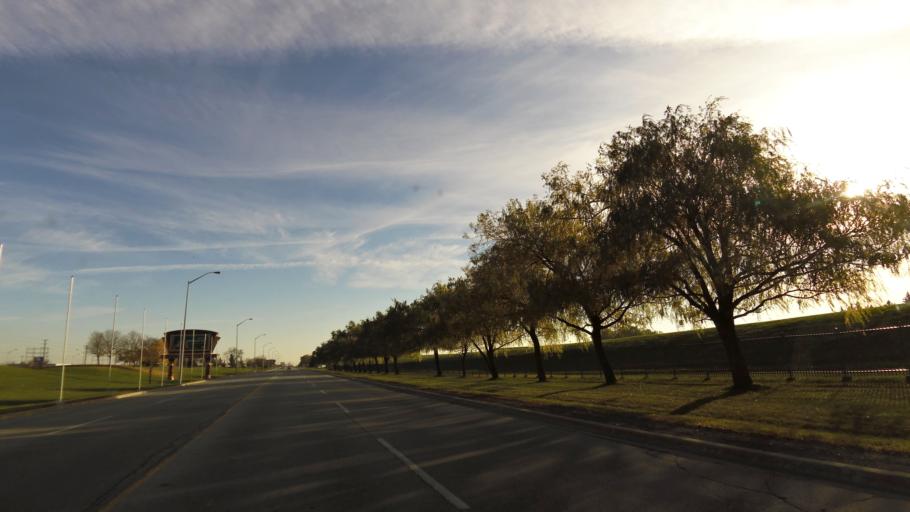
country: CA
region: Ontario
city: Etobicoke
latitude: 43.7139
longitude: -79.5953
